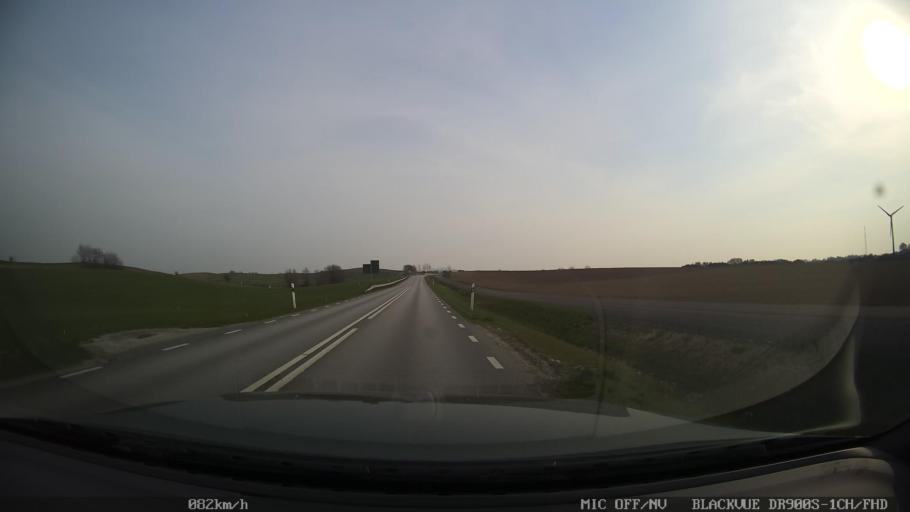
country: SE
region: Skane
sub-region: Ystads Kommun
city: Ystad
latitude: 55.4664
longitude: 13.7989
